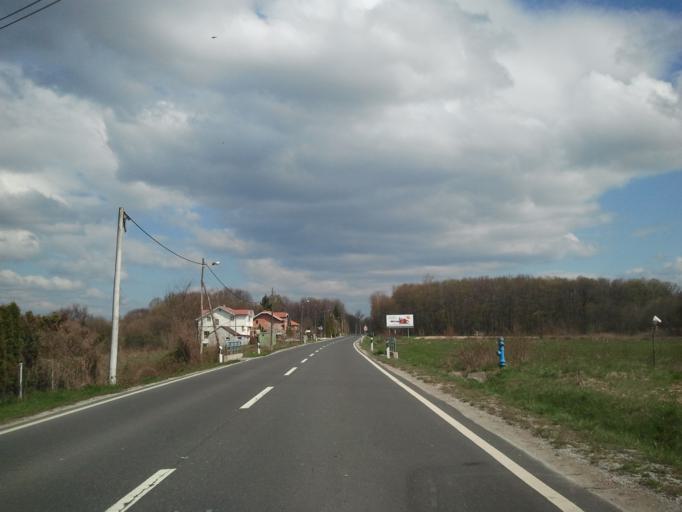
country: HR
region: Grad Zagreb
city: Horvati
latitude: 45.7156
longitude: 15.7791
